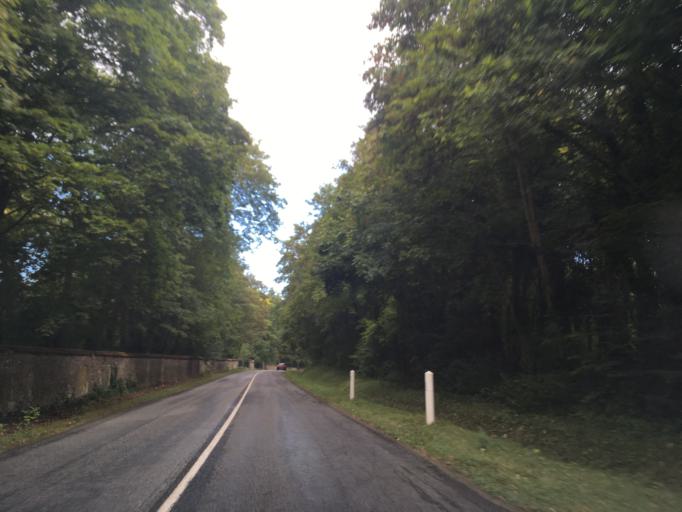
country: FR
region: Haute-Normandie
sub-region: Departement de l'Eure
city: Saint-Just
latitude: 49.1211
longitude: 1.4582
